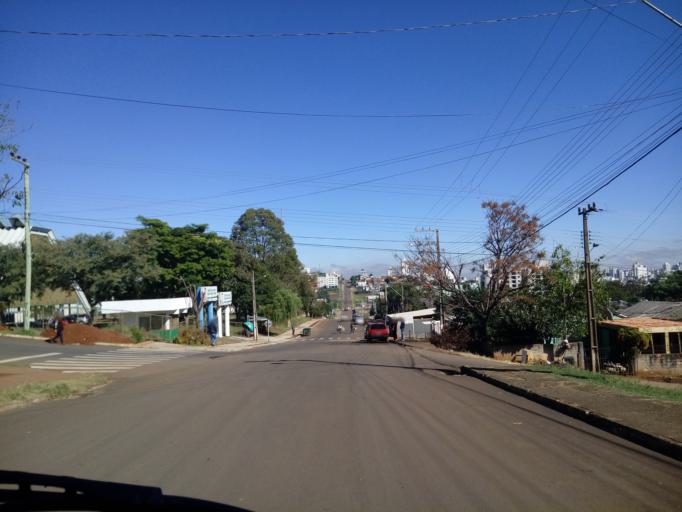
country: BR
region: Santa Catarina
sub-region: Chapeco
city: Chapeco
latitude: -27.0999
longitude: -52.5924
